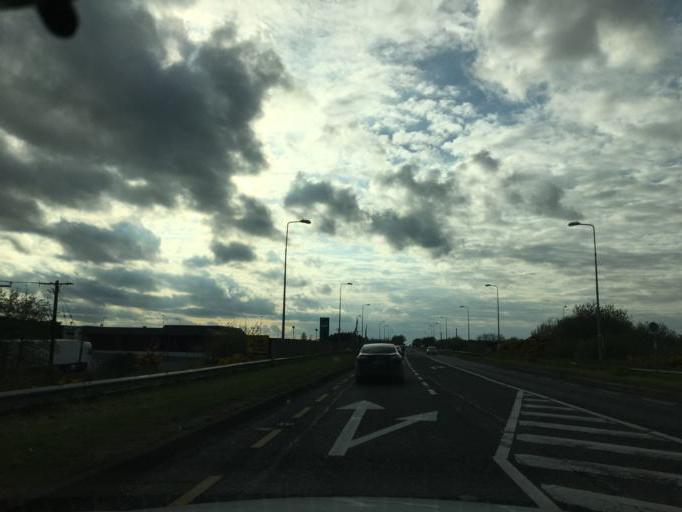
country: IE
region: Leinster
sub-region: Loch Garman
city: Loch Garman
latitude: 52.3395
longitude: -6.5624
